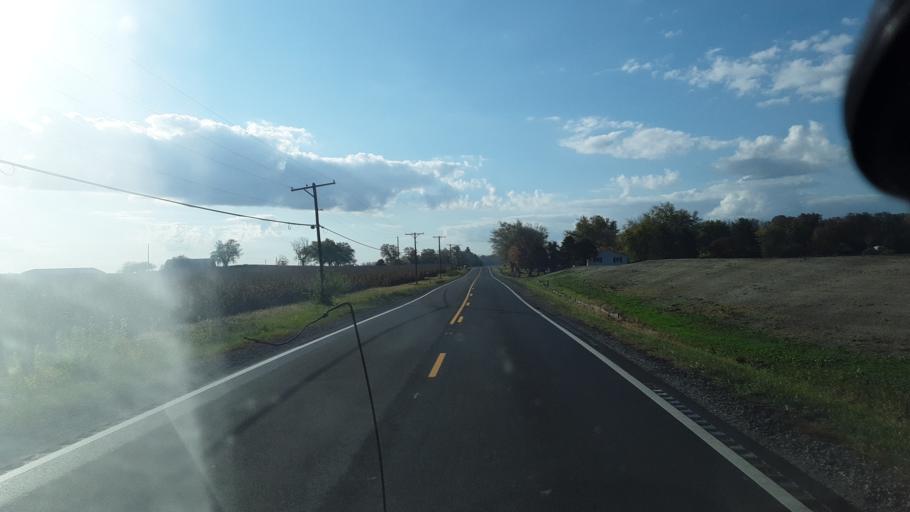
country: US
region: Ohio
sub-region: Fayette County
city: Jeffersonville
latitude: 39.6183
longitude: -83.5276
